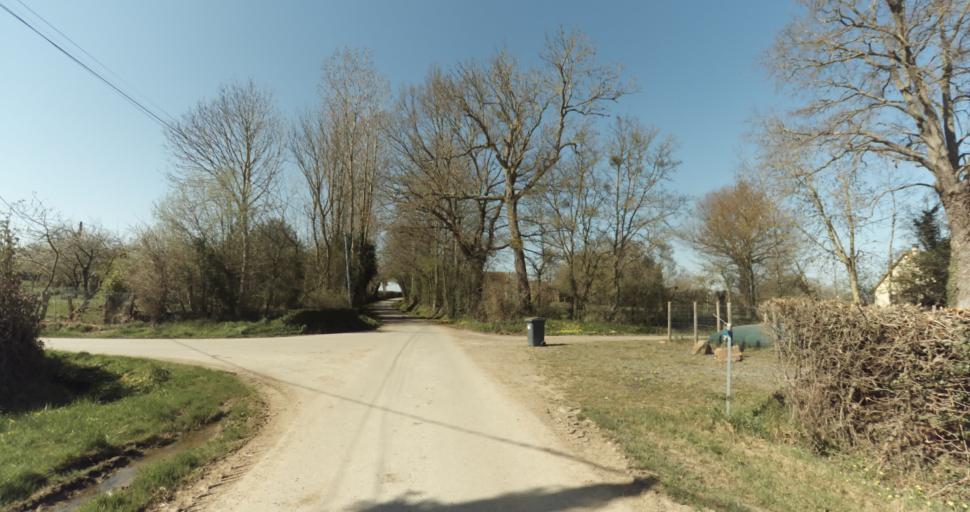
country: FR
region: Lower Normandy
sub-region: Departement du Calvados
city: Saint-Pierre-sur-Dives
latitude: 49.0125
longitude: -0.0023
